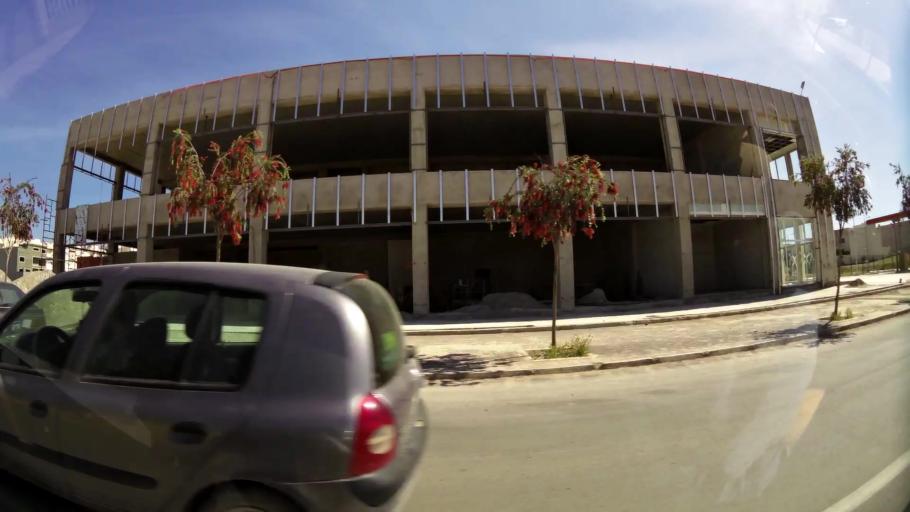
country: MA
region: Oriental
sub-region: Oujda-Angad
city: Oujda
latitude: 34.6550
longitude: -1.9123
